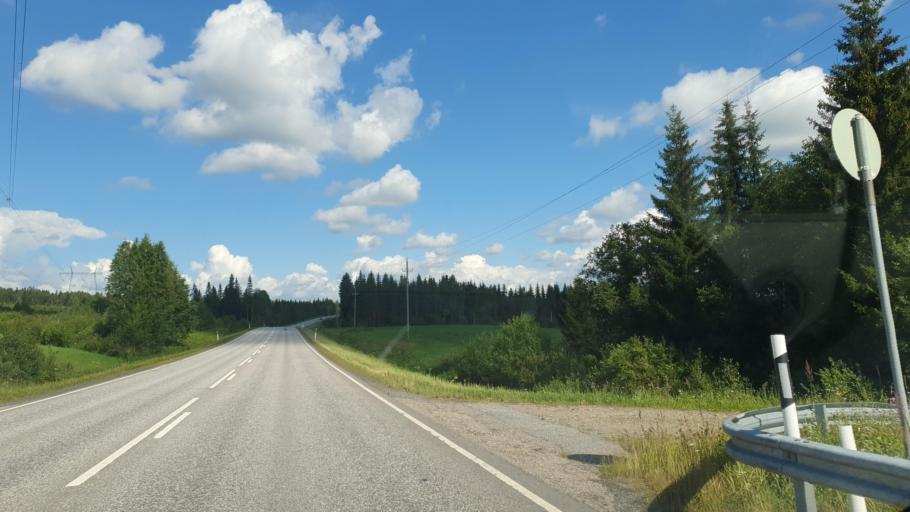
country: FI
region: Northern Savo
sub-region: Ylae-Savo
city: Sonkajaervi
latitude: 63.7067
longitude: 27.3582
